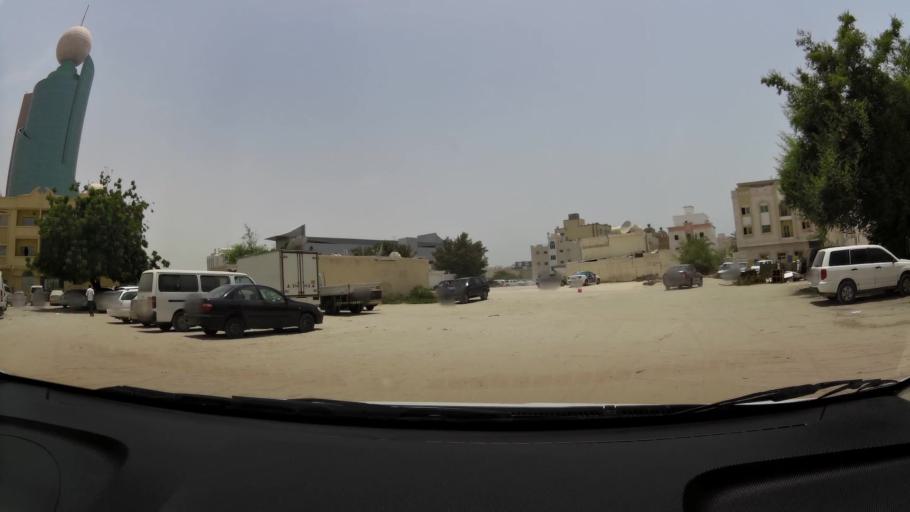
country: AE
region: Ash Shariqah
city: Sharjah
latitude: 25.3563
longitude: 55.3997
